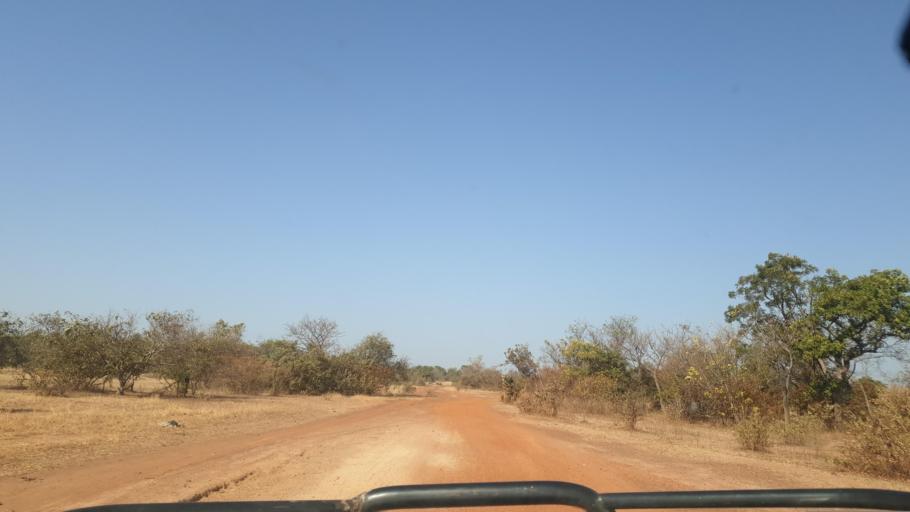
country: ML
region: Sikasso
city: Bougouni
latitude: 11.8188
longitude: -6.9456
